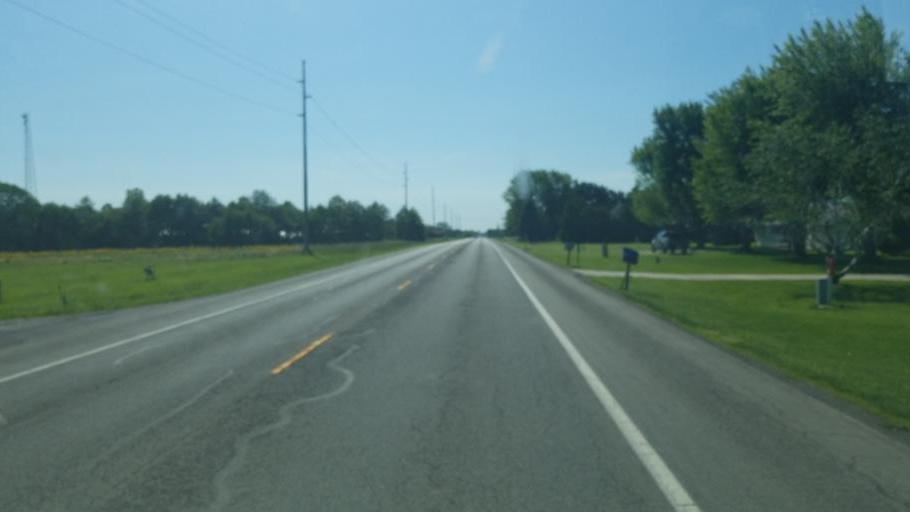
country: US
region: Ohio
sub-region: Hardin County
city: Kenton
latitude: 40.6590
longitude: -83.6416
